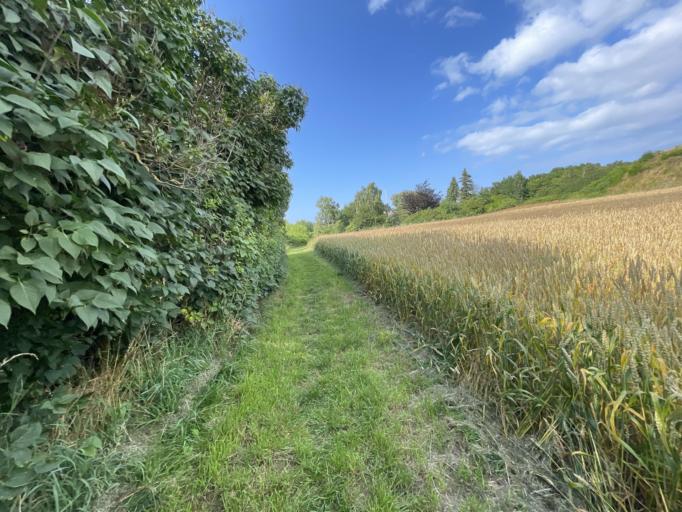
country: DK
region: Capital Region
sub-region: Gribskov Kommune
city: Helsinge
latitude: 56.0892
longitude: 12.1788
